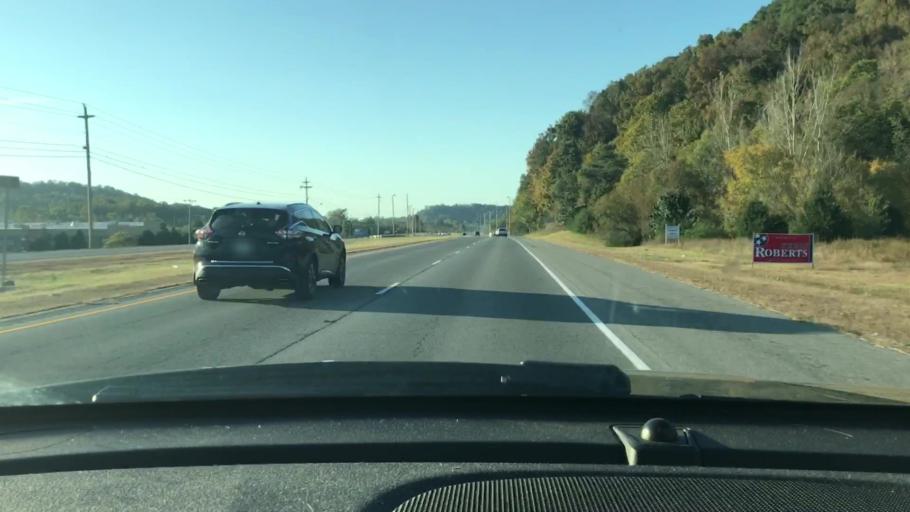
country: US
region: Tennessee
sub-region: Cheatham County
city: Ashland City
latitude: 36.2475
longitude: -87.0291
